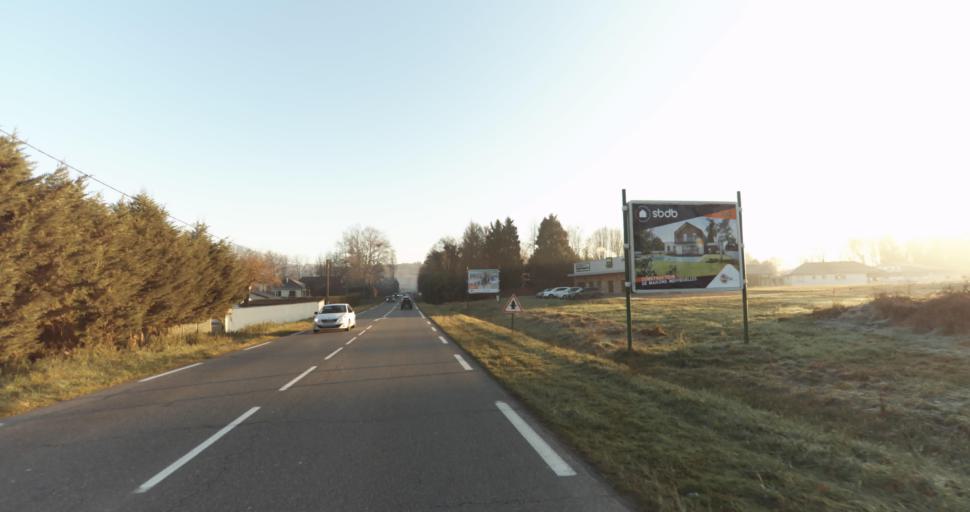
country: FR
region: Aquitaine
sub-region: Departement des Pyrenees-Atlantiques
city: Buros
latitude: 43.3252
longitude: -0.2946
